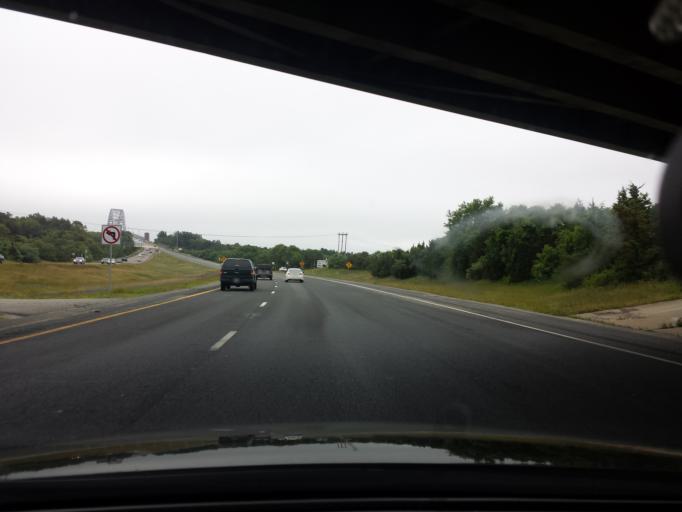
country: US
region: Massachusetts
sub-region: Barnstable County
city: Bourne
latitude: 41.7566
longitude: -70.5945
